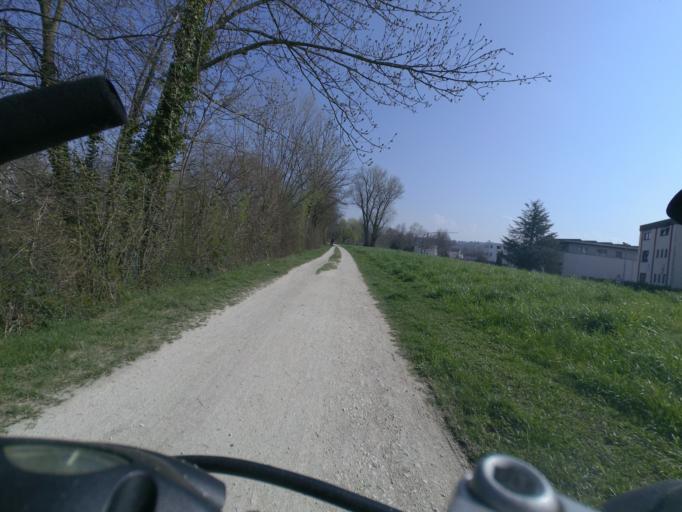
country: DE
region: Baden-Wuerttemberg
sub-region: Regierungsbezirk Stuttgart
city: Nurtingen
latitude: 48.6393
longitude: 9.3432
